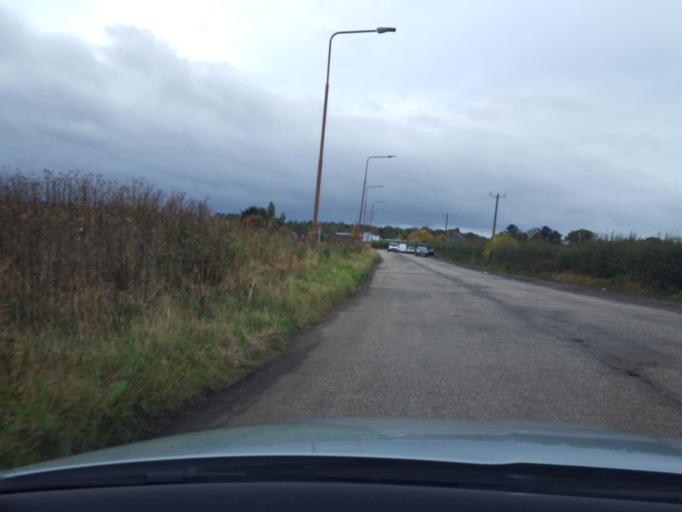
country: GB
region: Scotland
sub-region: Edinburgh
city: Currie
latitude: 55.9198
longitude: -3.3109
